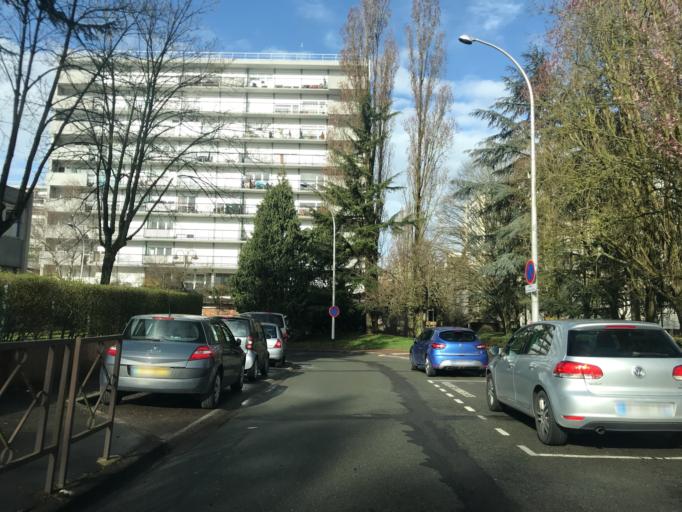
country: FR
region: Ile-de-France
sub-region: Departement des Yvelines
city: Velizy-Villacoublay
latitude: 48.7814
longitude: 2.1995
